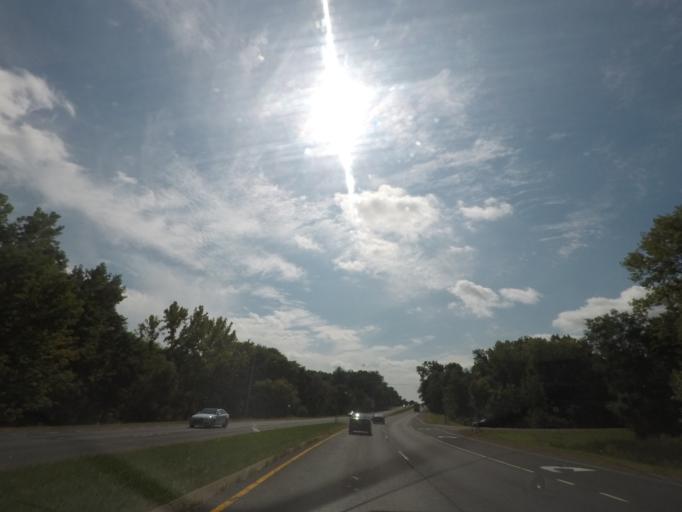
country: US
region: New York
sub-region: Albany County
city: Delmar
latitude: 42.6320
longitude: -73.8513
